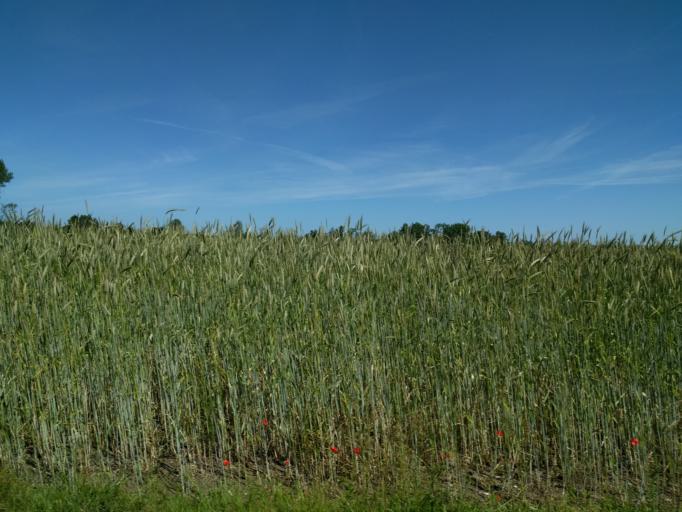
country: DK
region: South Denmark
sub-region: Kerteminde Kommune
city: Langeskov
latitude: 55.3420
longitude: 10.5920
